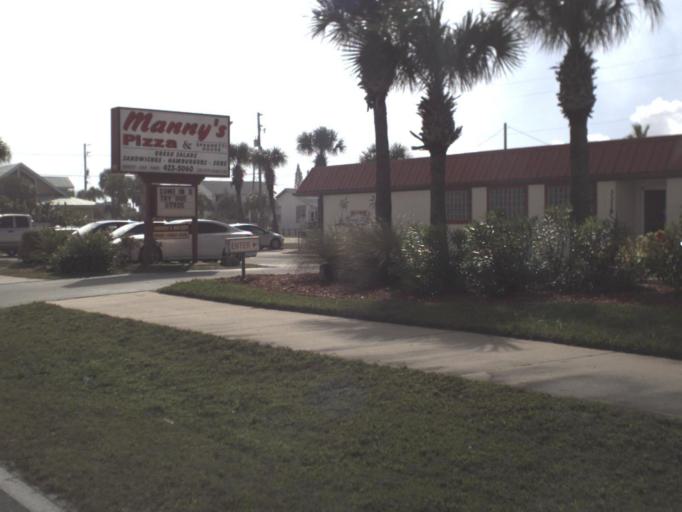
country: US
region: Florida
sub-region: Volusia County
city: Edgewater
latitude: 29.0121
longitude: -80.8813
